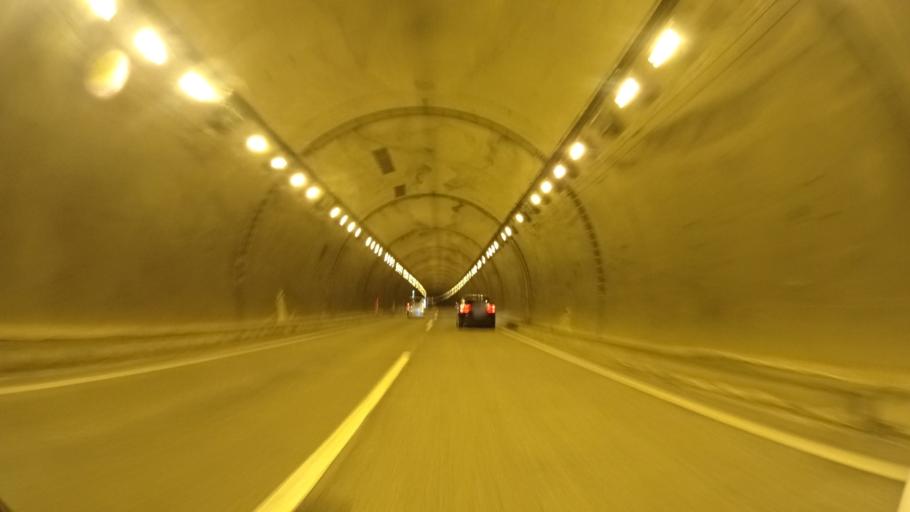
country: JP
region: Ehime
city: Niihama
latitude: 33.9187
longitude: 133.3130
